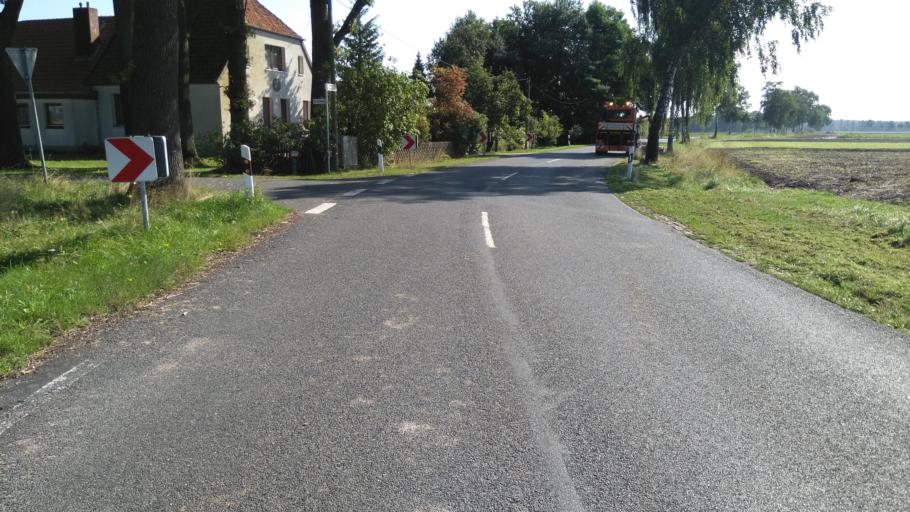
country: DE
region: Lower Saxony
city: Walsrode
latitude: 52.8998
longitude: 9.5996
